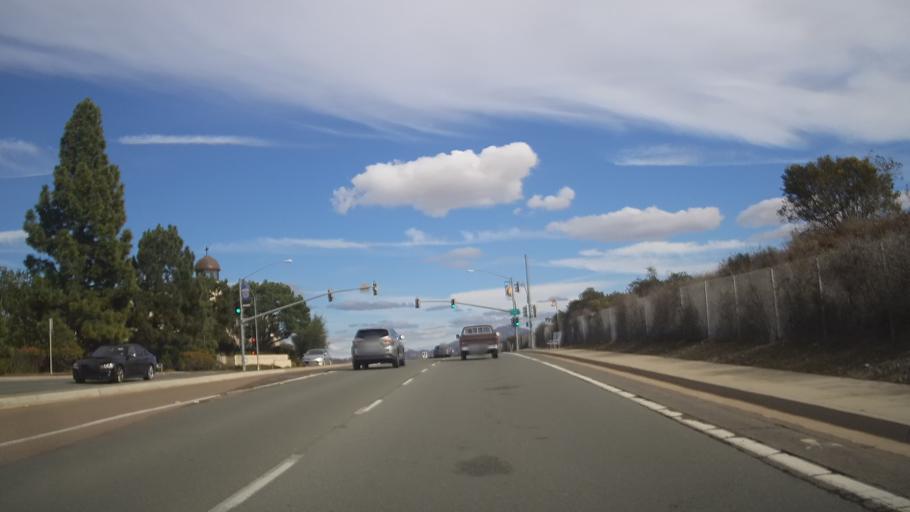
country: US
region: California
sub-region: San Diego County
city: Poway
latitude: 32.9622
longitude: -117.1045
